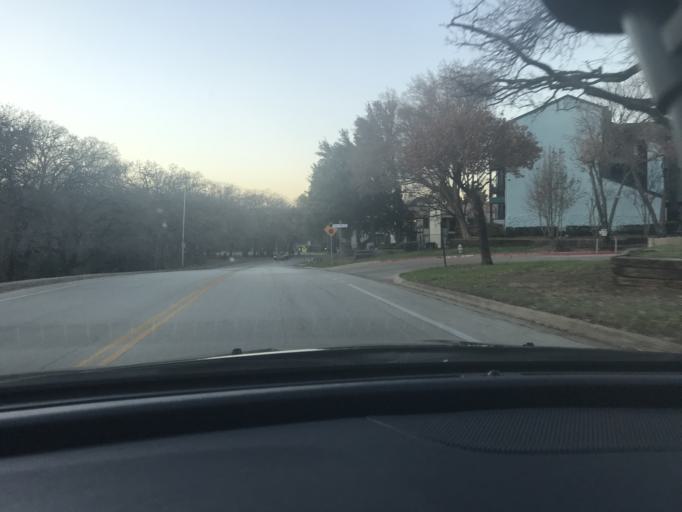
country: US
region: Texas
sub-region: Tarrant County
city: Arlington
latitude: 32.7659
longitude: -97.1047
